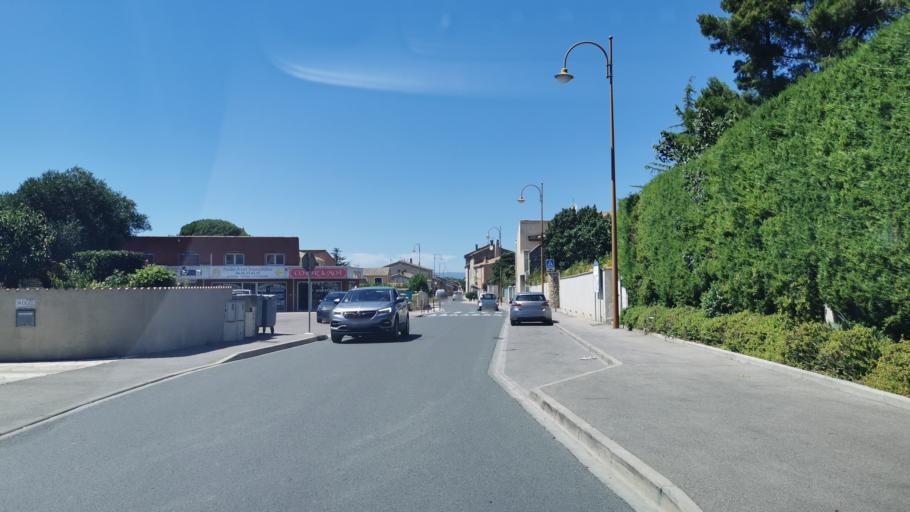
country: FR
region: Languedoc-Roussillon
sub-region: Departement de l'Aude
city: Fleury
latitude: 43.2340
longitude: 3.1227
